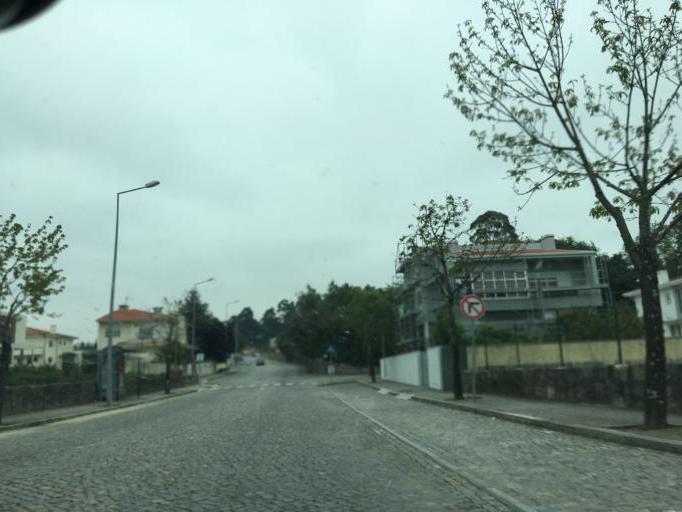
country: PT
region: Porto
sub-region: Maia
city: Nogueira
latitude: 41.2459
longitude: -8.5997
